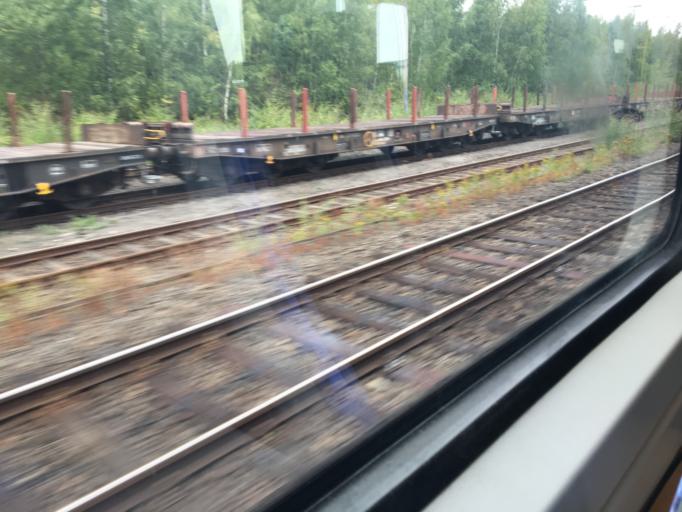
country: DE
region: North Rhine-Westphalia
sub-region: Regierungsbezirk Arnsberg
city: Dortmund
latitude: 51.5049
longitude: 7.4321
